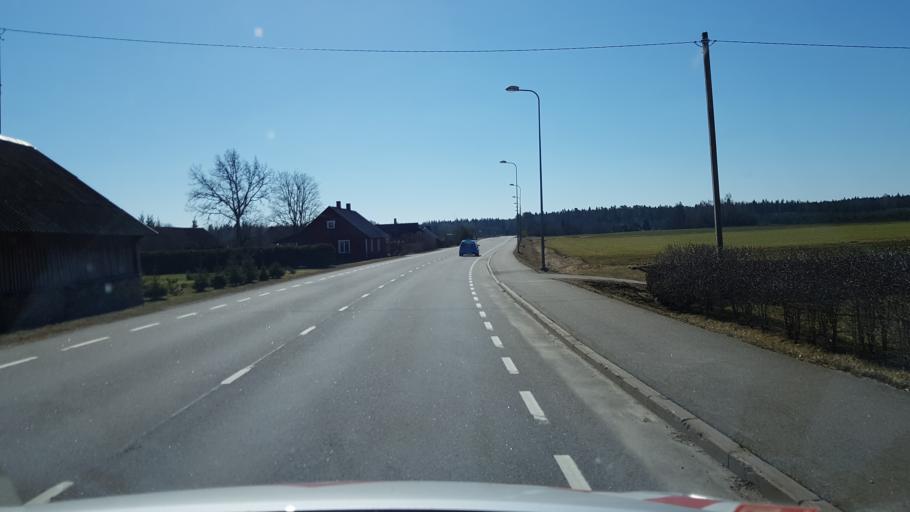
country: EE
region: Laeaene-Virumaa
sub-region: Vinni vald
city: Vinni
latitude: 59.1477
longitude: 26.5944
